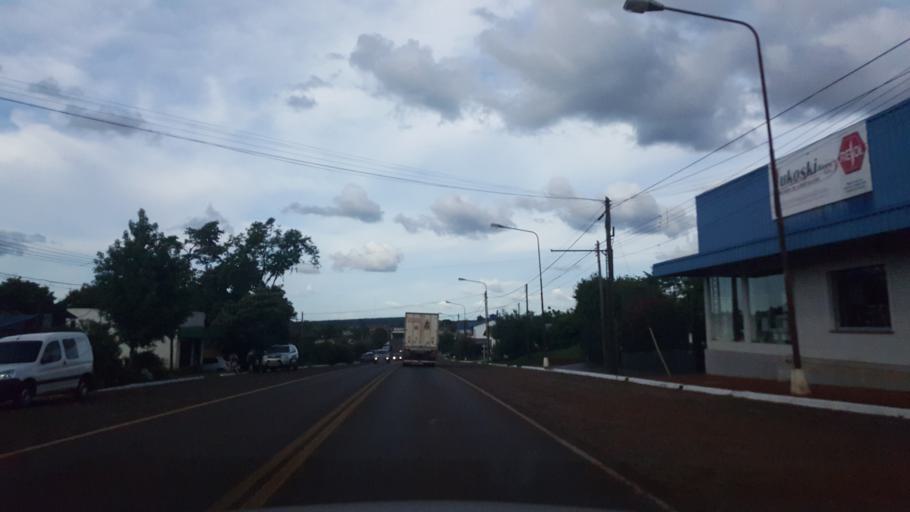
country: AR
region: Misiones
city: Gobernador Roca
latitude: -27.1882
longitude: -55.4665
